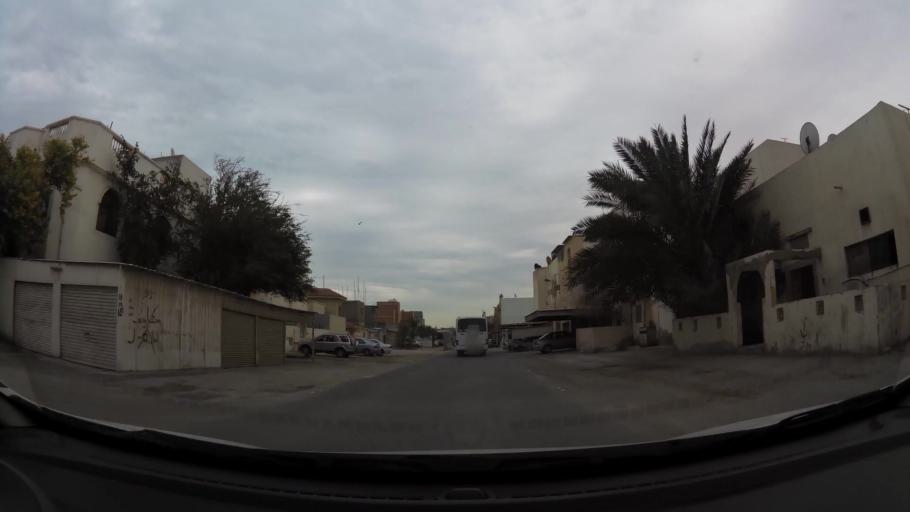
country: BH
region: Northern
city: Sitrah
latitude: 26.1685
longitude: 50.6074
